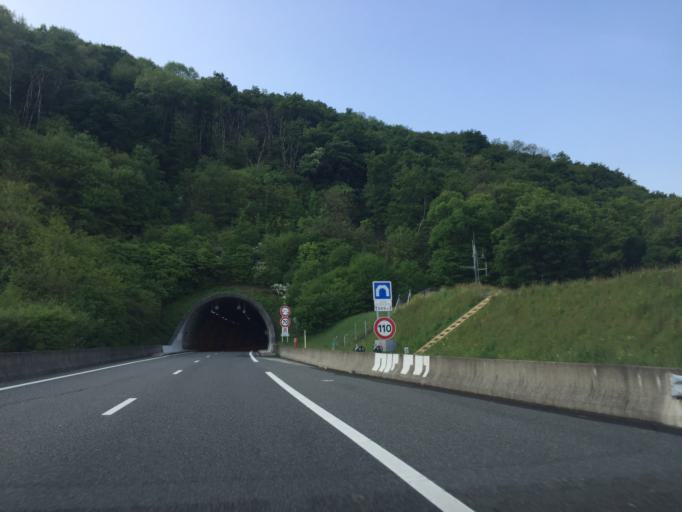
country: FR
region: Rhone-Alpes
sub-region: Departement de l'Isere
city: Vif
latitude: 45.0552
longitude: 5.6861
